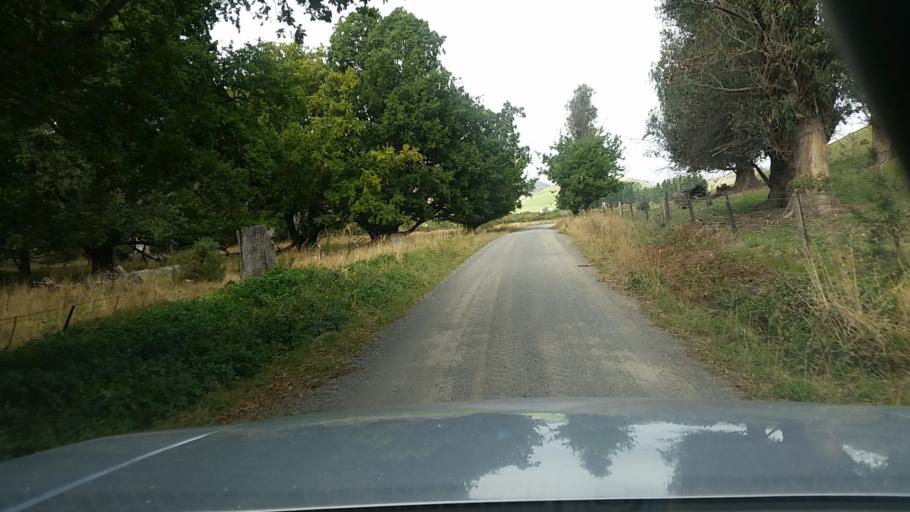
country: NZ
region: Marlborough
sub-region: Marlborough District
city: Blenheim
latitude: -41.7369
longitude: 173.8927
